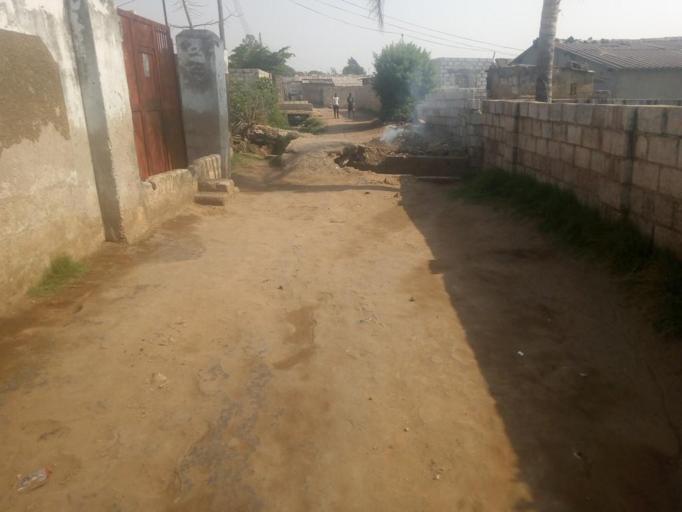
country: ZM
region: Lusaka
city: Lusaka
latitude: -15.4054
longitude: 28.3614
